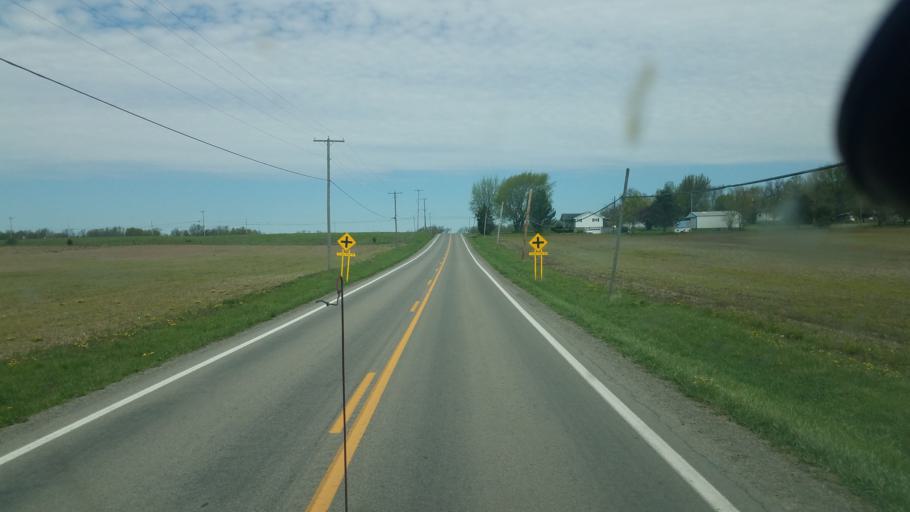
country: US
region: Ohio
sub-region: Hardin County
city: Ada
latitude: 40.7050
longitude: -83.7852
